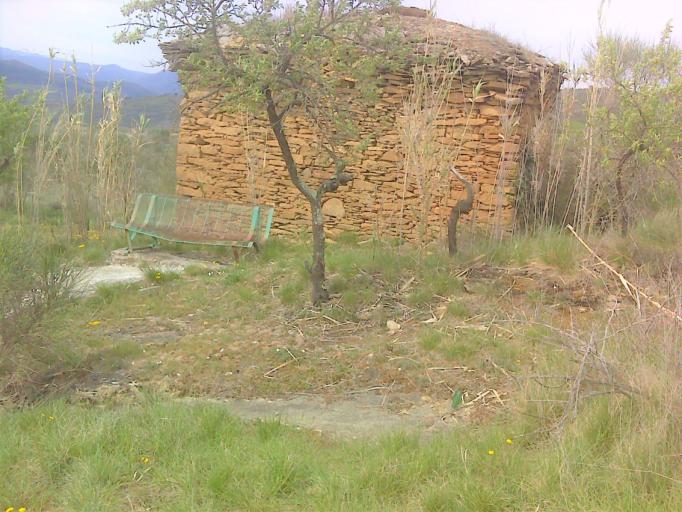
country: FR
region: Languedoc-Roussillon
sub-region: Departement de l'Aude
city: Esperaza
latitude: 42.9434
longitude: 2.2142
